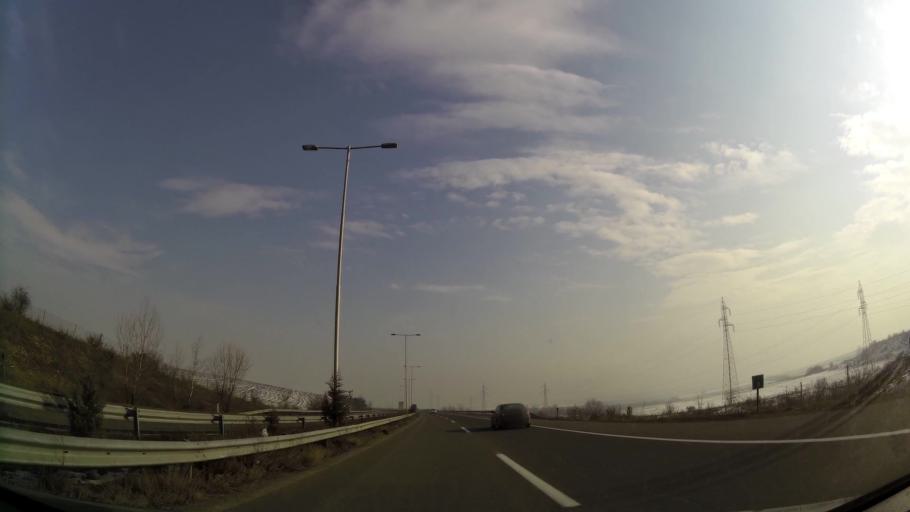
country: MK
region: Butel
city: Butel
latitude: 42.0337
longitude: 21.4733
